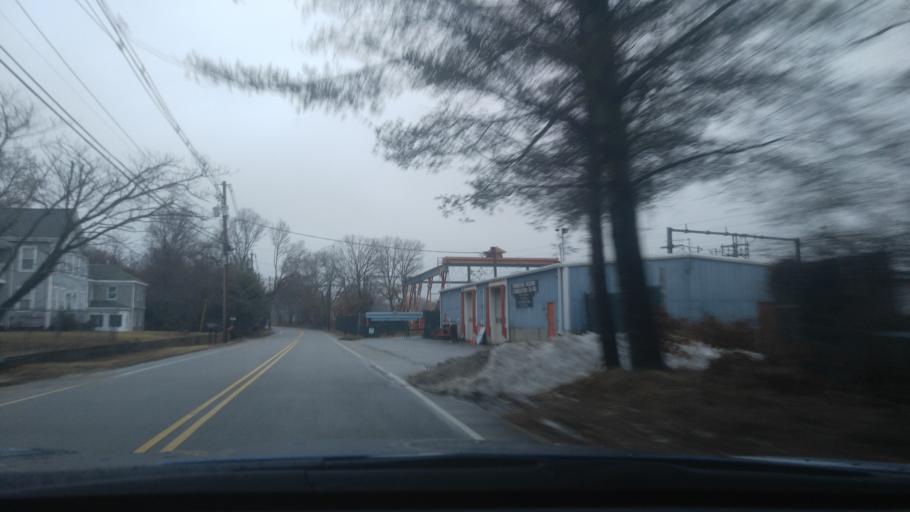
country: US
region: Rhode Island
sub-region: Kent County
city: East Greenwich
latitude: 41.6103
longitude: -71.4773
